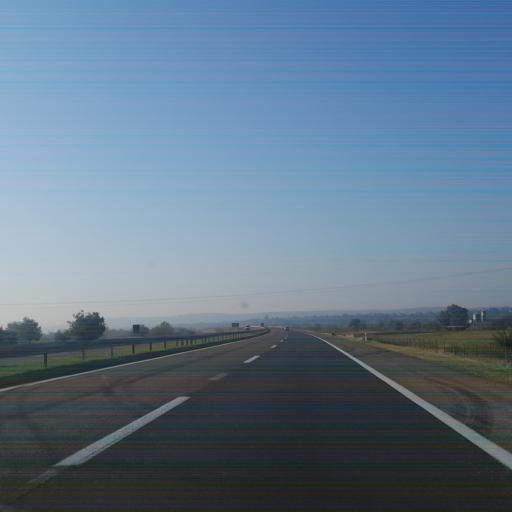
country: RS
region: Central Serbia
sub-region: Nisavski Okrug
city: Merosina
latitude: 43.3091
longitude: 21.8001
